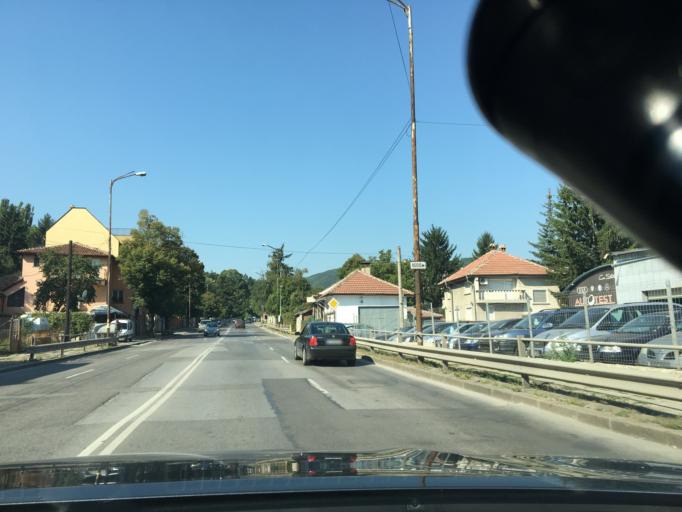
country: BG
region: Sofia-Capital
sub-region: Stolichna Obshtina
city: Sofia
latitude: 42.6568
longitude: 23.2352
